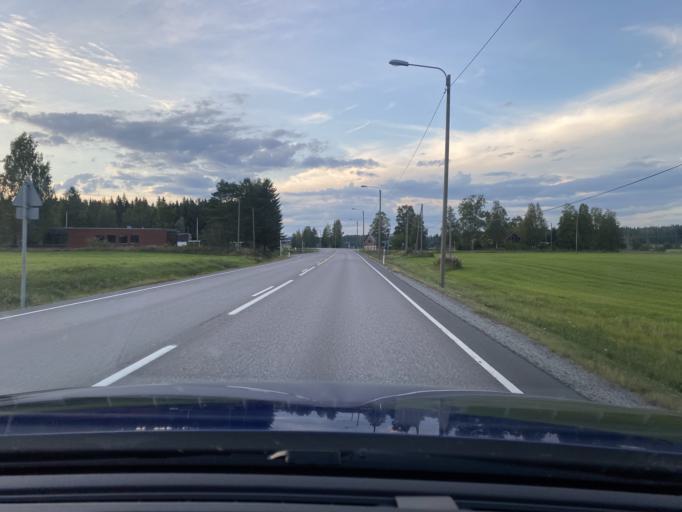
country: FI
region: Satakunta
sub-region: Pohjois-Satakunta
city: Kankaanpaeae
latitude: 61.7414
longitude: 22.5250
